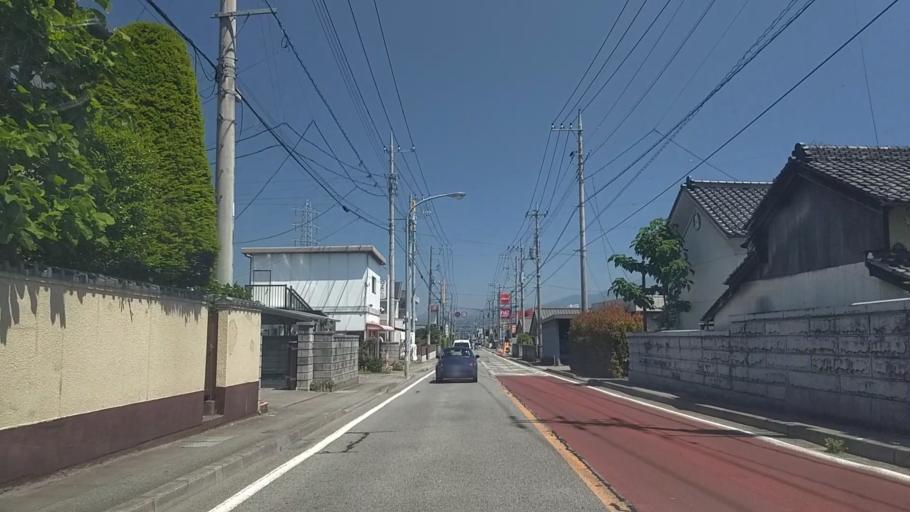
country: JP
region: Yamanashi
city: Ryuo
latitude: 35.6590
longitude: 138.4650
